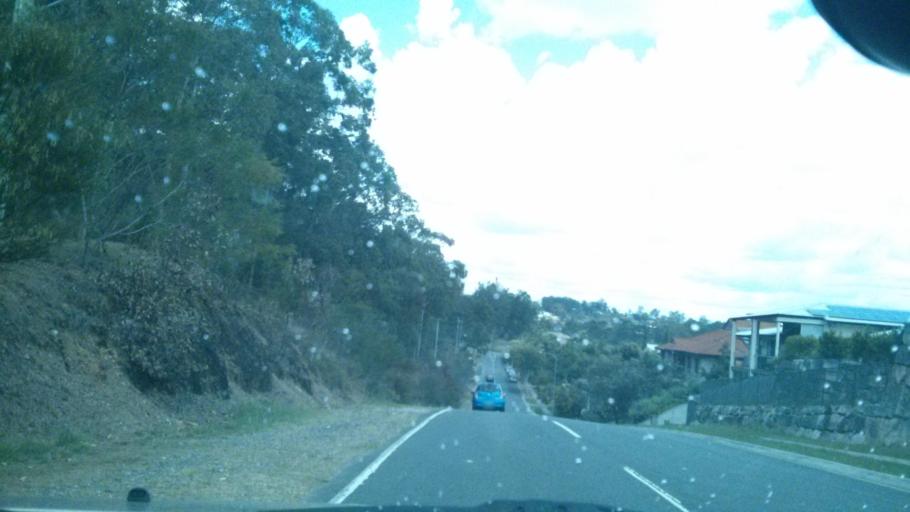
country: AU
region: Queensland
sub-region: Brisbane
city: Kenmore Hills
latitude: -27.4906
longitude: 152.9443
